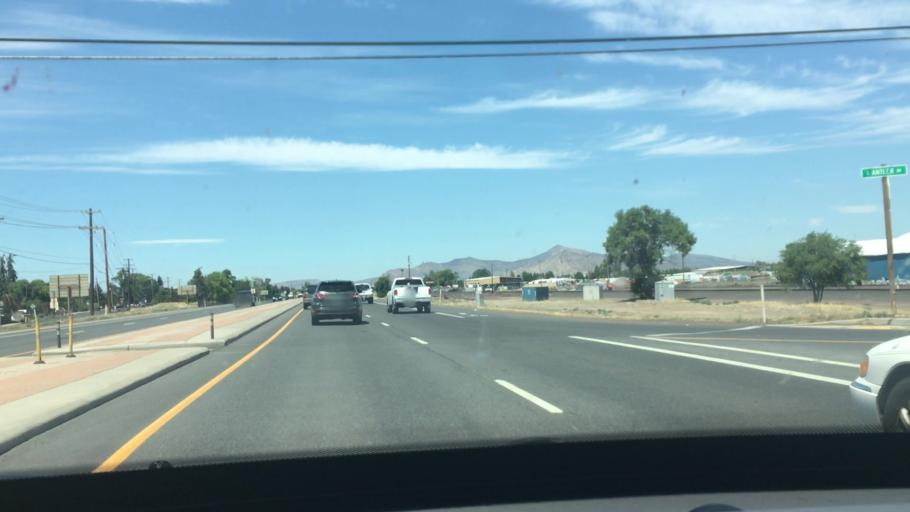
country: US
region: Oregon
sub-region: Deschutes County
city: Redmond
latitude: 44.2766
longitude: -121.1688
